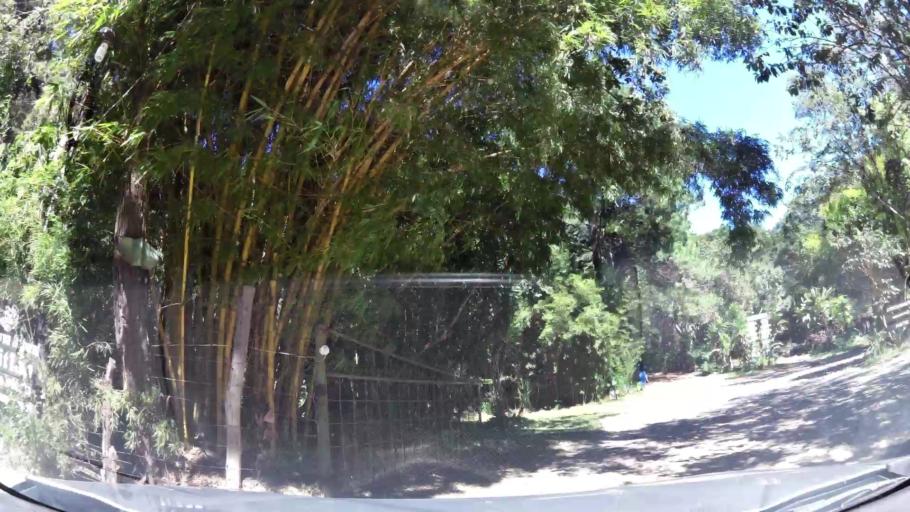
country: GT
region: Solola
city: Panajachel
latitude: 14.7507
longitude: -91.1661
